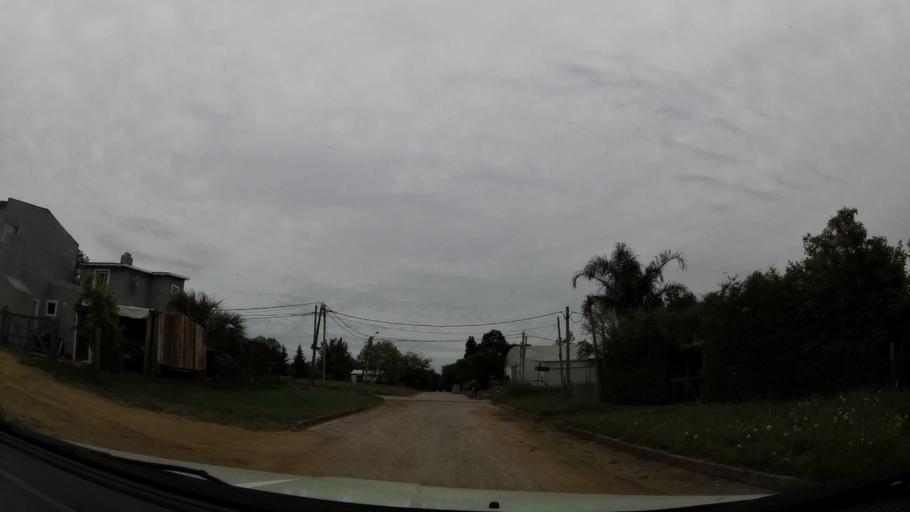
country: UY
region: Maldonado
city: Maldonado
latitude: -34.8801
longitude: -54.9847
